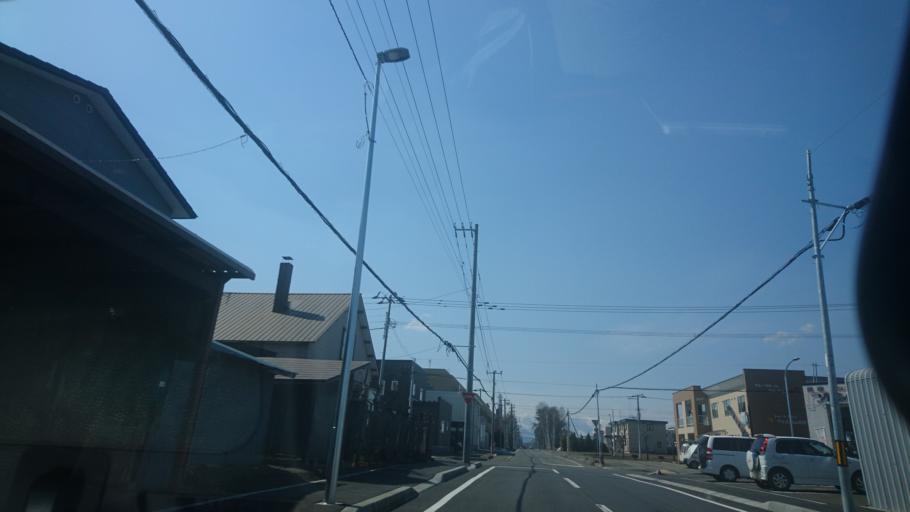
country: JP
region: Hokkaido
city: Obihiro
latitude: 42.9136
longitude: 143.0567
